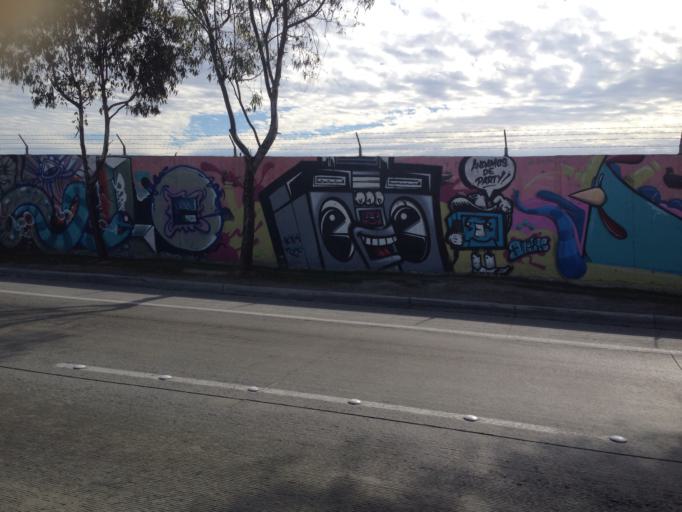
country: MX
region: Baja California
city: Tijuana
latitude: 32.5464
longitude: -116.9820
